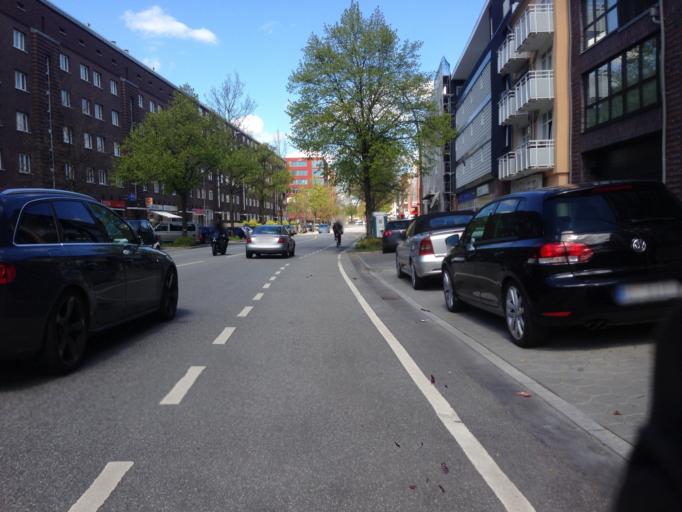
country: DE
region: Hamburg
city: Barmbek-Nord
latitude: 53.5995
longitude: 10.0414
